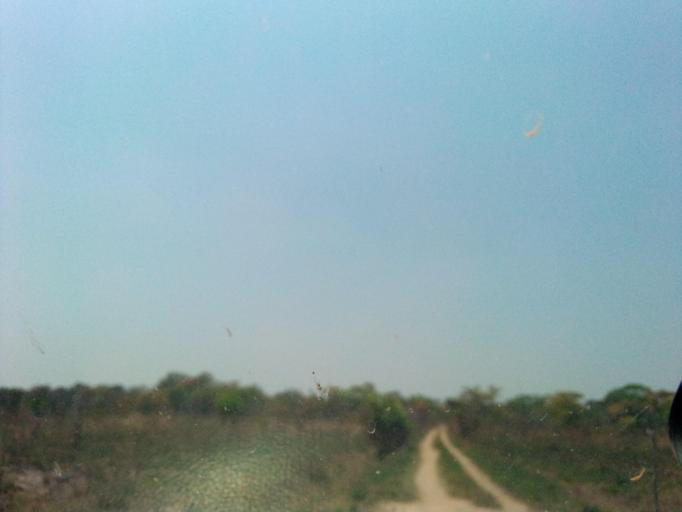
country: ZM
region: Copperbelt
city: Kataba
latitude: -12.2463
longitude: 30.3958
